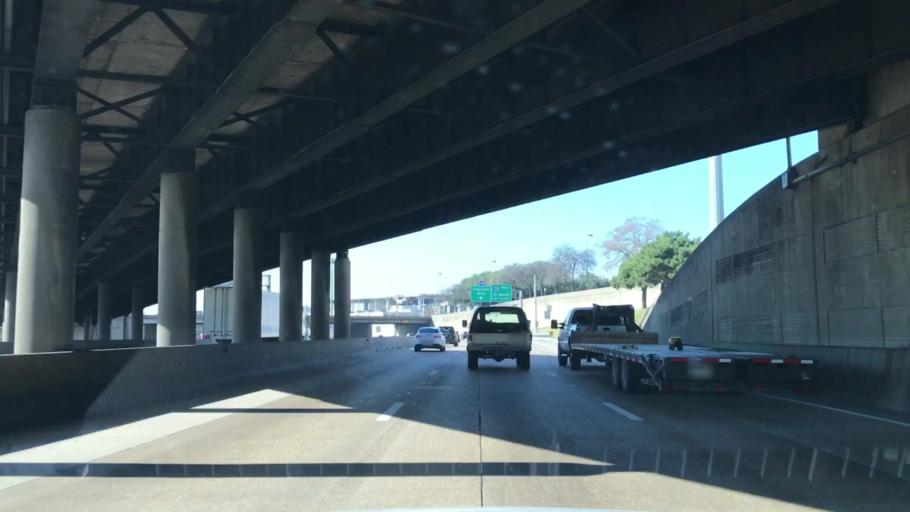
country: US
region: Texas
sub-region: Dallas County
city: Dallas
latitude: 32.7735
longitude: -96.7966
